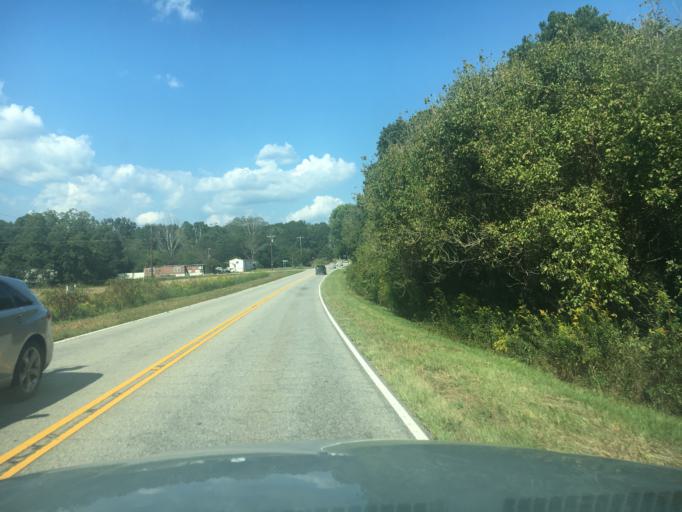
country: US
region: South Carolina
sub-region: Anderson County
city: Pendleton
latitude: 34.6092
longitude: -82.7893
